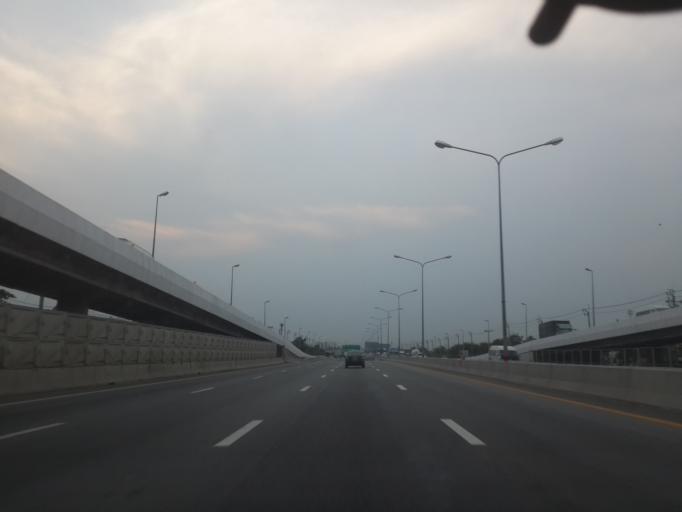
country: TH
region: Bangkok
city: Lat Krabang
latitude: 13.7320
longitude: 100.7767
